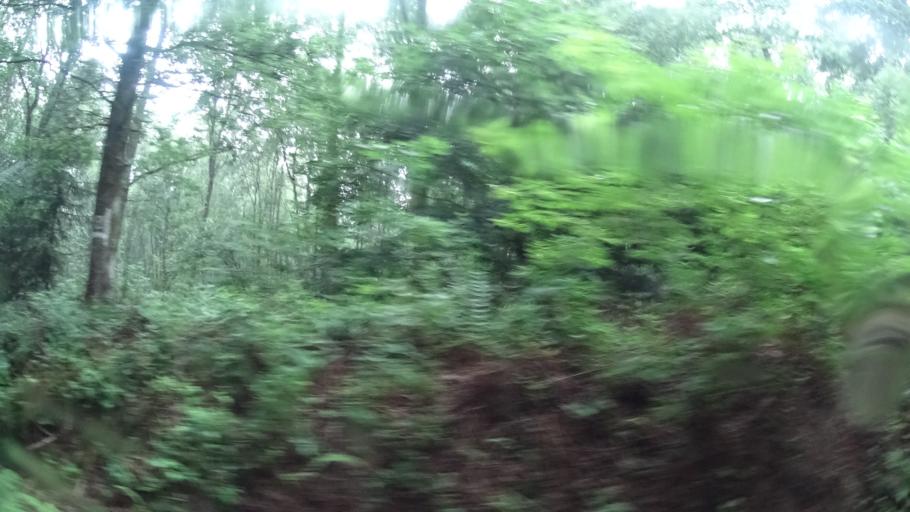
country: BE
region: Wallonia
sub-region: Province de Namur
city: Bievre
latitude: 49.9825
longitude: 5.0111
